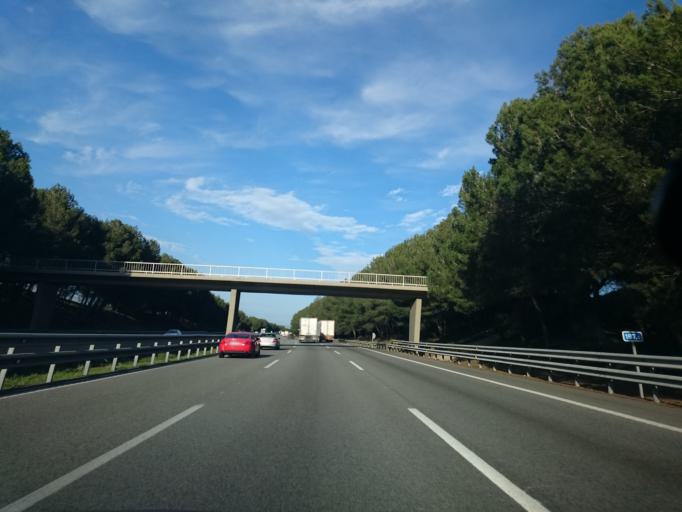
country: ES
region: Catalonia
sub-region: Provincia de Barcelona
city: Sant Sadurni d'Anoia
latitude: 41.3892
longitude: 1.7601
